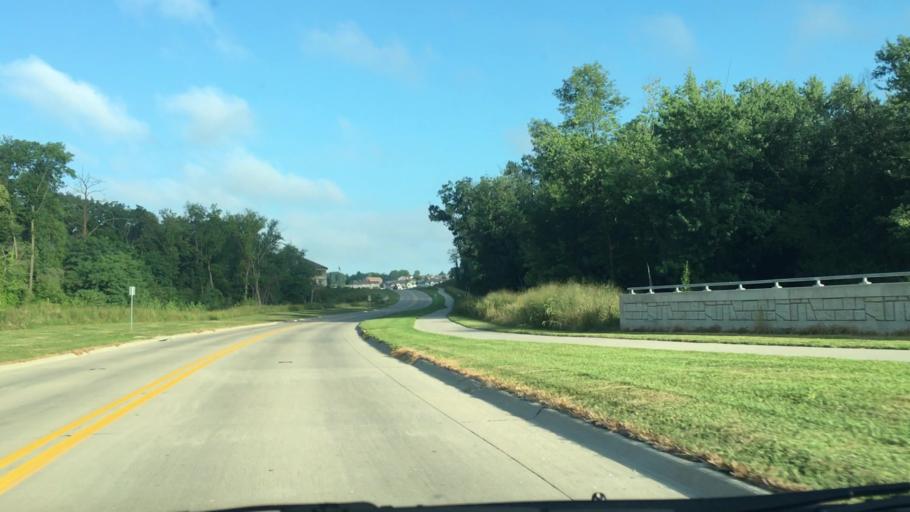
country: US
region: Iowa
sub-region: Johnson County
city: Coralville
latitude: 41.6997
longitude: -91.5493
